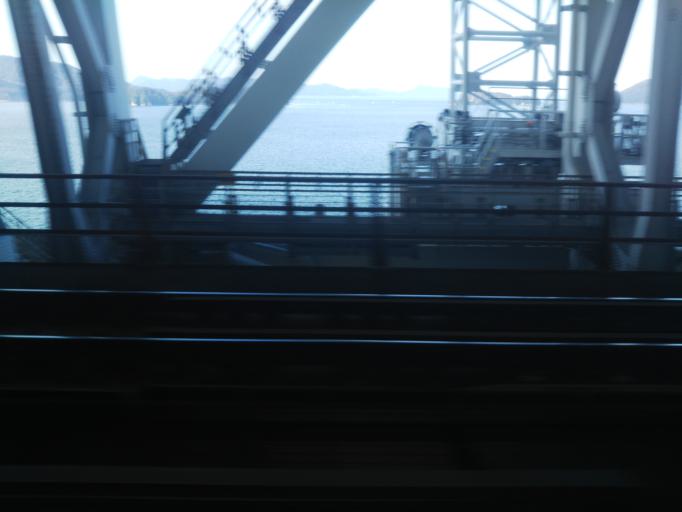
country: JP
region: Kagawa
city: Sakaidecho
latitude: 34.4132
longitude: 133.8059
